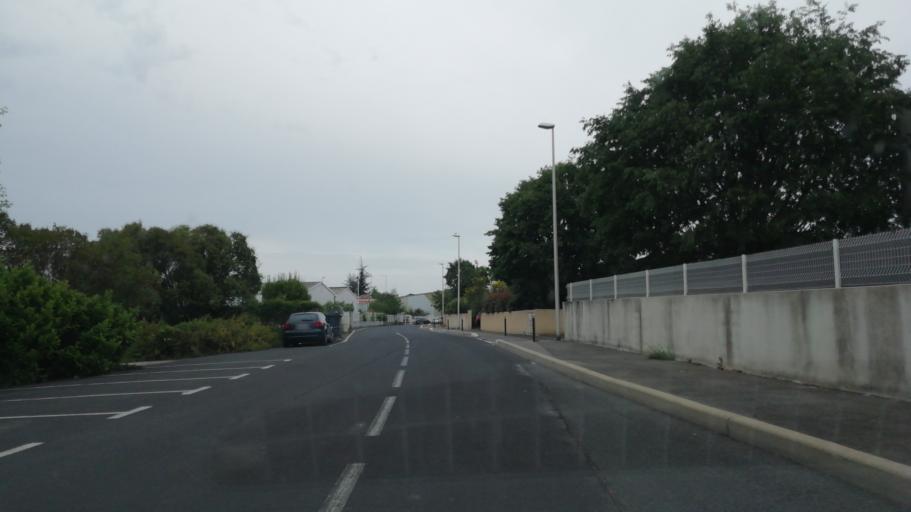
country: FR
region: Languedoc-Roussillon
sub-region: Departement de l'Herault
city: Saint-Mathieu-de-Treviers
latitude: 43.7644
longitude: 3.8707
